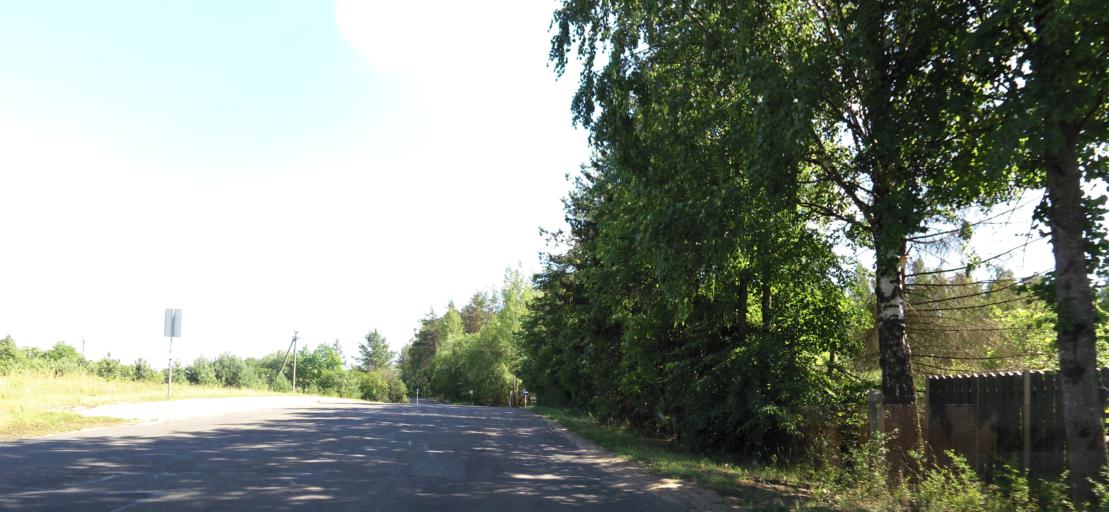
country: LT
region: Vilnius County
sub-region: Vilnius
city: Fabijoniskes
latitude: 54.8035
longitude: 25.3294
